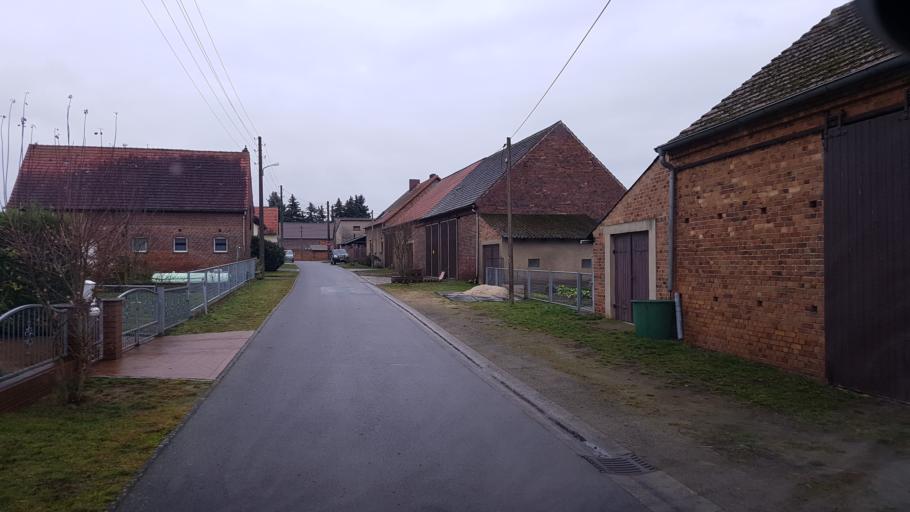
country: DE
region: Brandenburg
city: Altdobern
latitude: 51.6943
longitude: 14.0420
